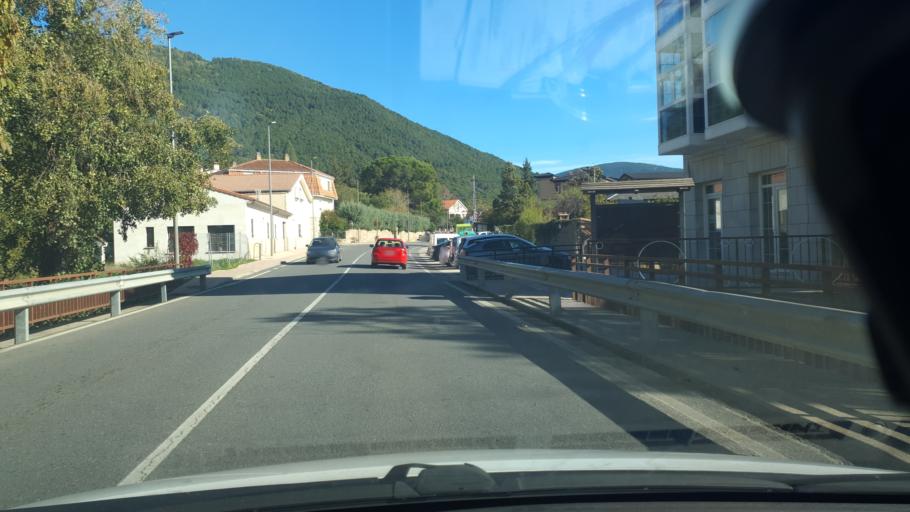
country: ES
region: Castille and Leon
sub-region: Provincia de Avila
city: Piedralaves
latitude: 40.3173
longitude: -4.6952
